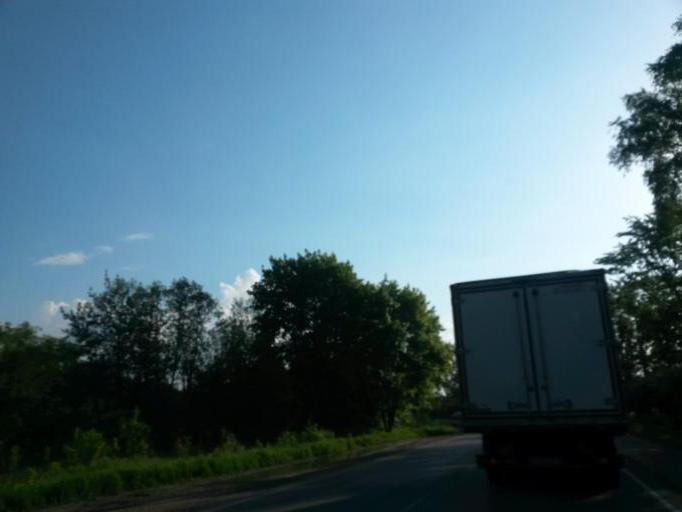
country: RU
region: Moskovskaya
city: Domodedovo
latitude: 55.4453
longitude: 37.6607
